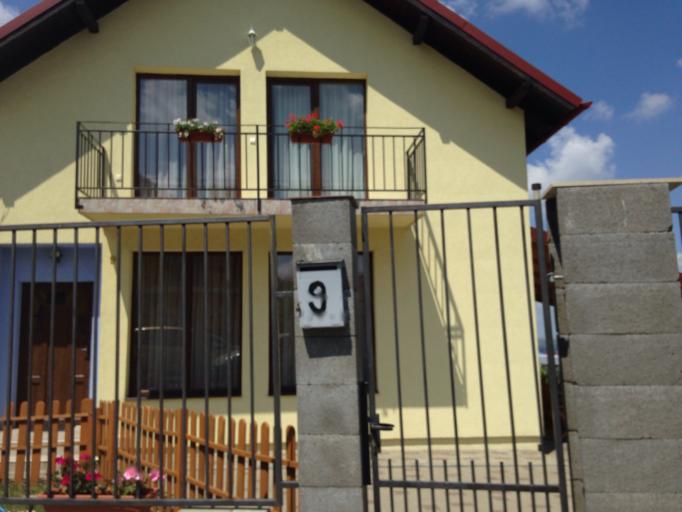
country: RO
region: Cluj
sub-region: Municipiul Cluj-Napoca
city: Cluj-Napoca
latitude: 46.7397
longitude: 23.5894
